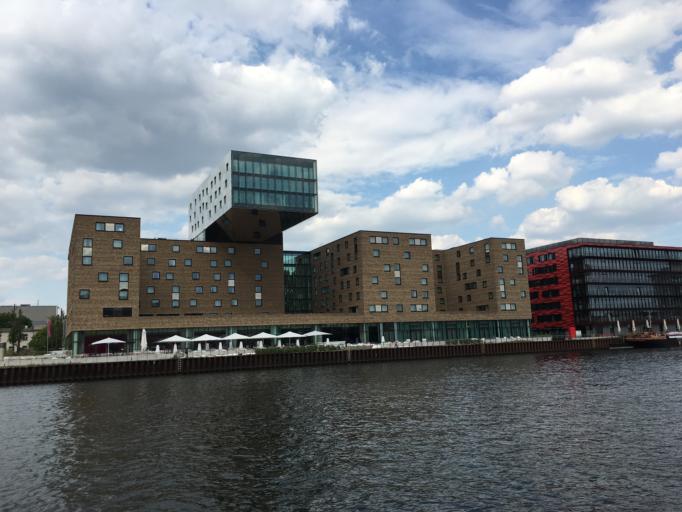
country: DE
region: Berlin
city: Berlin Treptow
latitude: 52.5003
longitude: 13.4493
